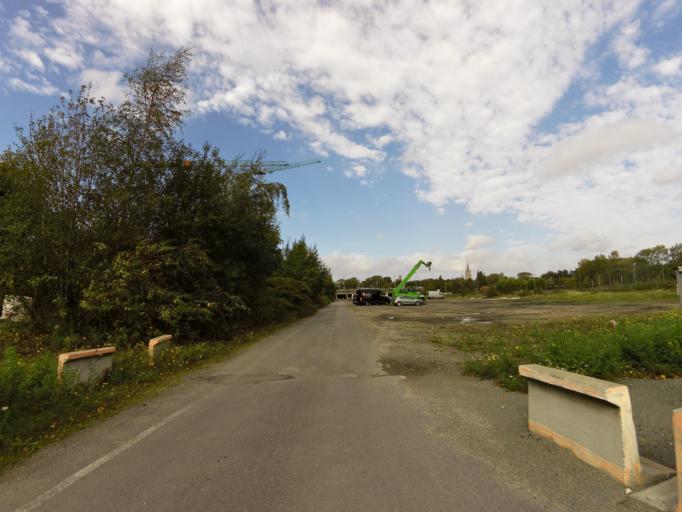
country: BE
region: Flanders
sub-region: Provincie West-Vlaanderen
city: Brugge
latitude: 51.1939
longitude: 3.2217
